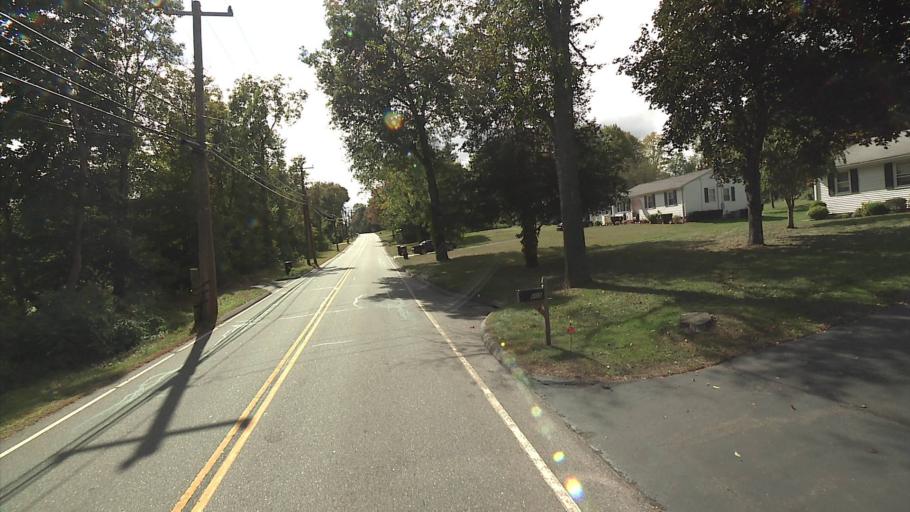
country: US
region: Connecticut
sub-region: Middlesex County
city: Durham
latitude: 41.5052
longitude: -72.7169
